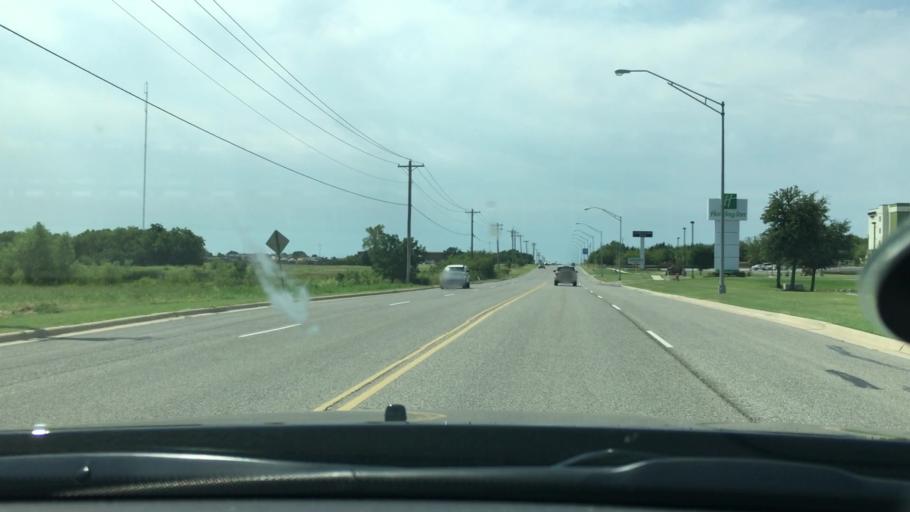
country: US
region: Oklahoma
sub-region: Carter County
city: Ardmore
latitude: 34.1990
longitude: -97.1605
